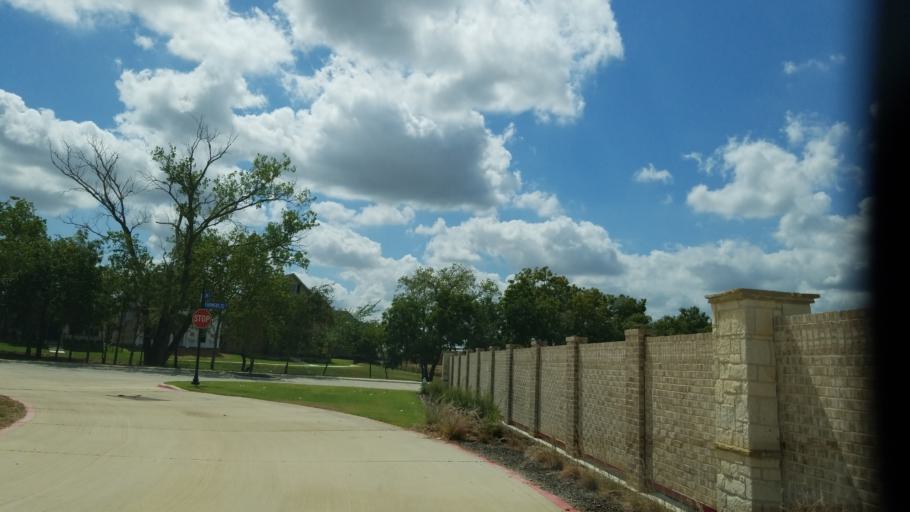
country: US
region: Texas
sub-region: Tarrant County
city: Euless
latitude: 32.8346
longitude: -97.0969
